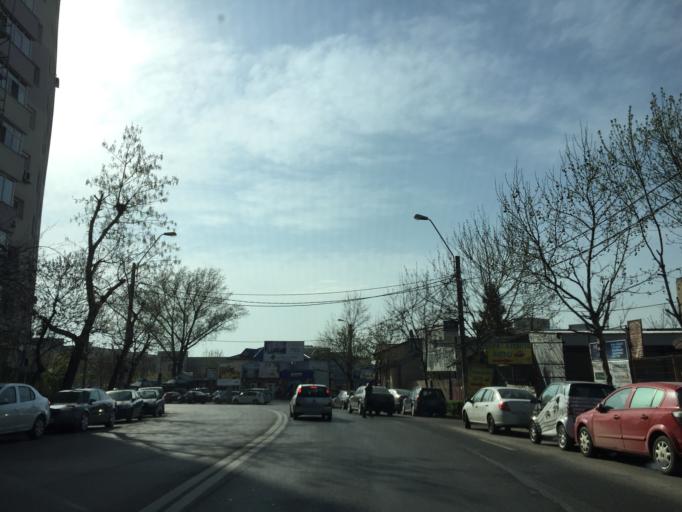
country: RO
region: Bucuresti
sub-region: Municipiul Bucuresti
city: Bucharest
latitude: 44.4096
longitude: 26.1374
